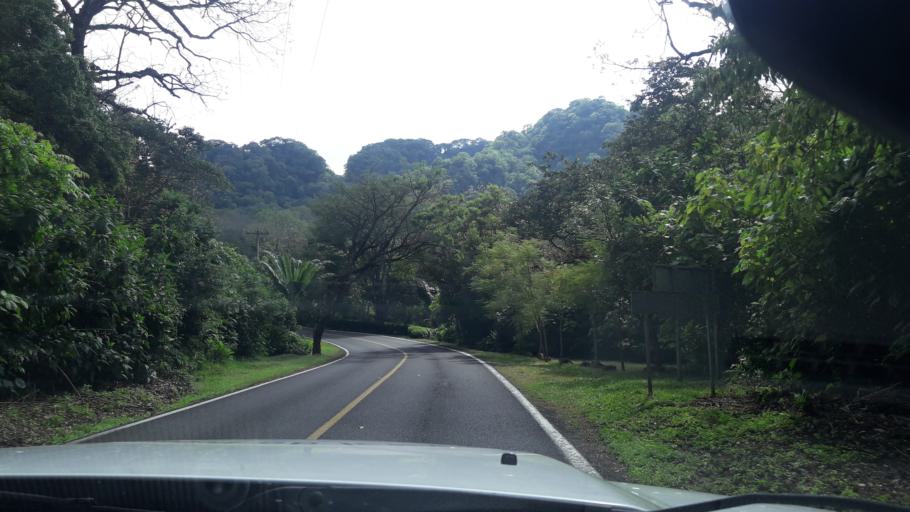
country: MX
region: Colima
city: Suchitlan
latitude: 19.4471
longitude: -103.7178
